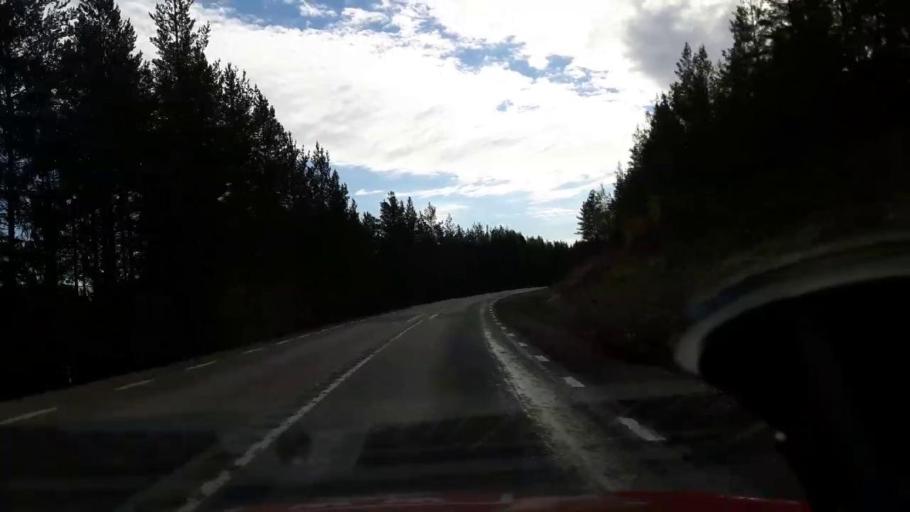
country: SE
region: Gaevleborg
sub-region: Ljusdals Kommun
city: Farila
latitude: 61.9455
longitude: 15.3776
